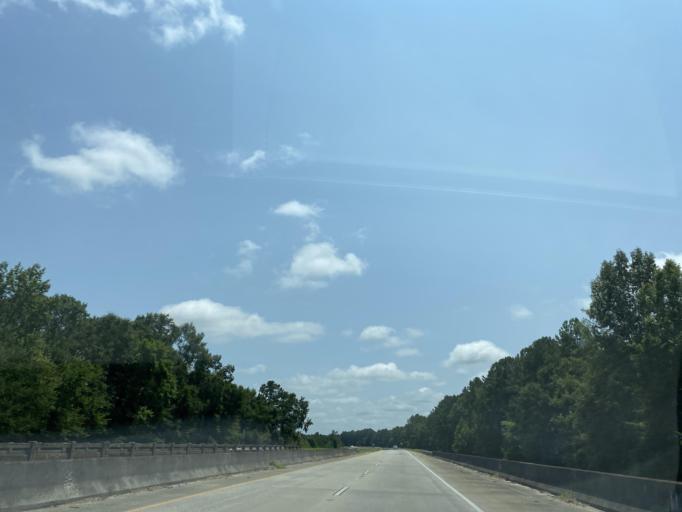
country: US
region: Georgia
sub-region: Telfair County
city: Lumber City
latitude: 31.9159
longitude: -82.6722
